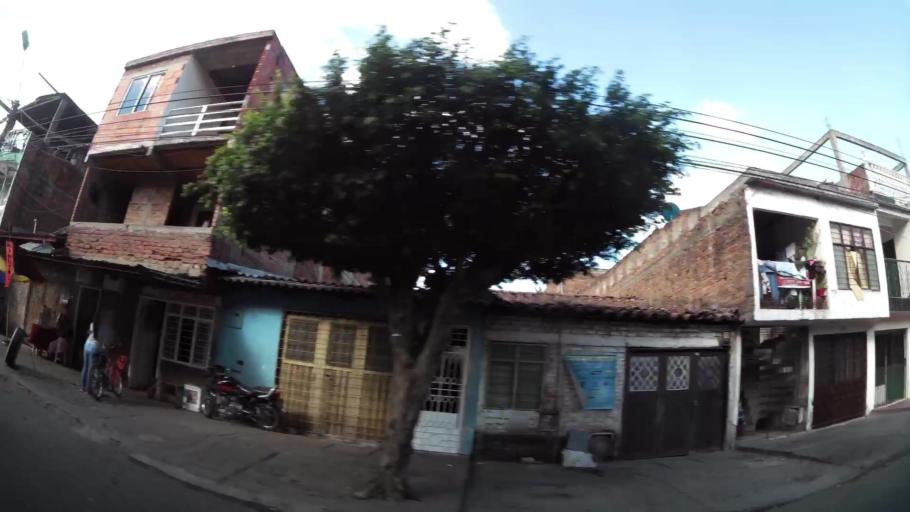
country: CO
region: Valle del Cauca
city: Cali
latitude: 3.4182
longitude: -76.4995
